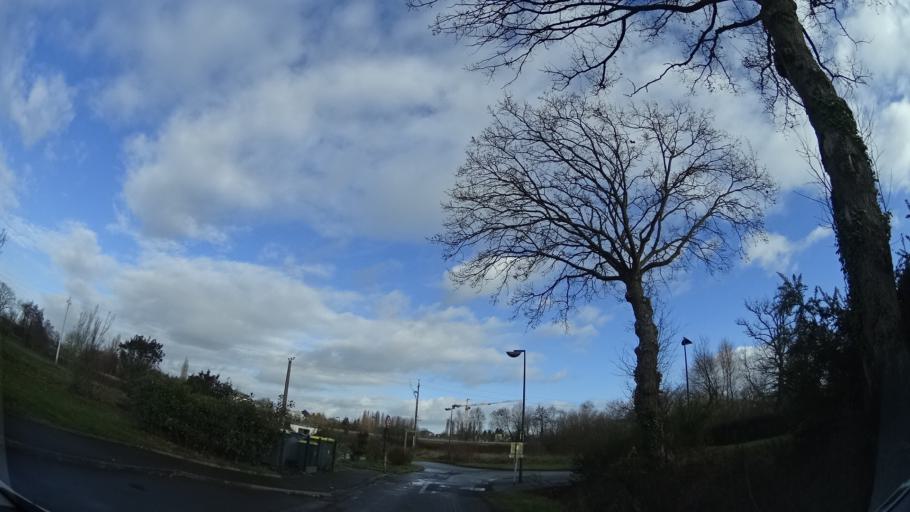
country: FR
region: Brittany
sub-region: Departement d'Ille-et-Vilaine
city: Chantepie
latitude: 48.0793
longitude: -1.6095
